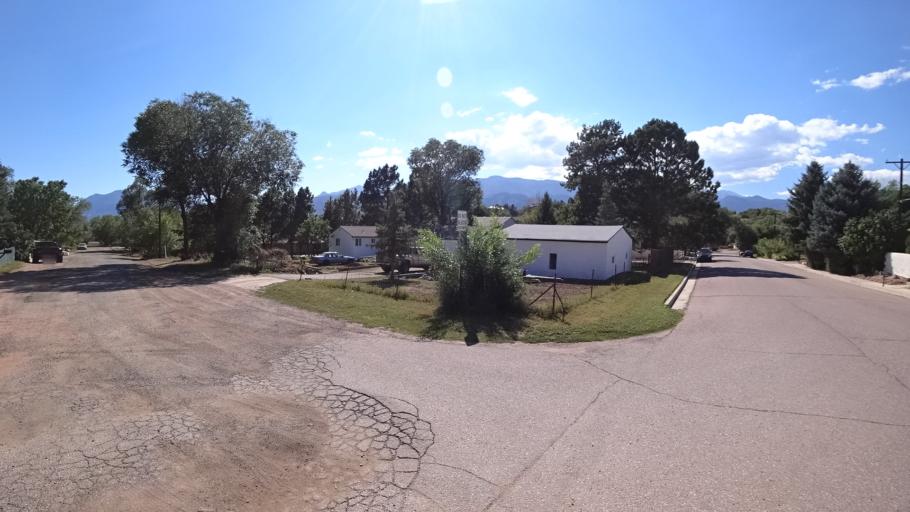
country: US
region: Colorado
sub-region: El Paso County
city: Colorado Springs
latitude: 38.8535
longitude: -104.8480
